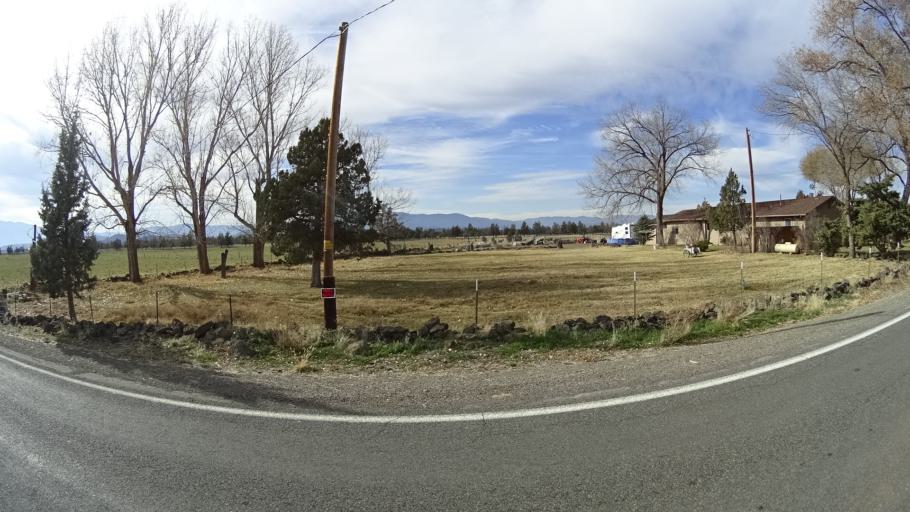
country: US
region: California
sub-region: Siskiyou County
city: Montague
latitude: 41.6300
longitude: -122.3995
